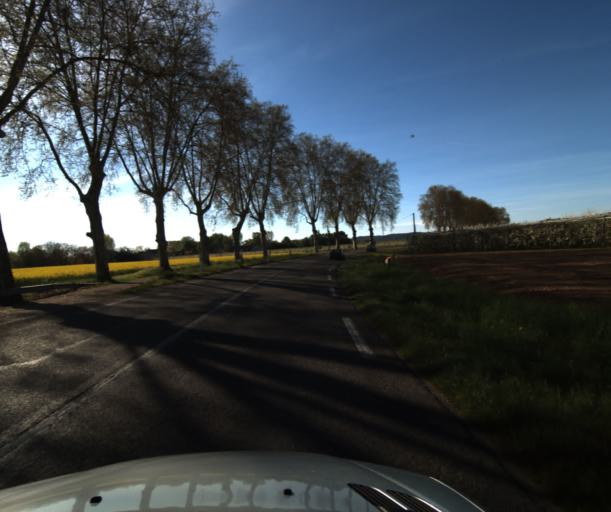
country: FR
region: Midi-Pyrenees
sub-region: Departement du Tarn-et-Garonne
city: Lafrancaise
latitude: 44.0896
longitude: 1.2672
